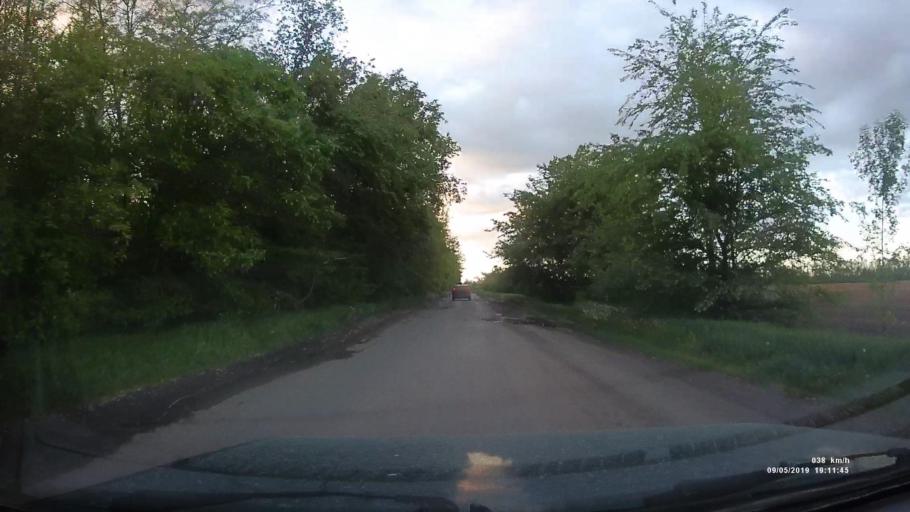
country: RU
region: Krasnodarskiy
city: Kanelovskaya
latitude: 46.7373
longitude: 39.2136
